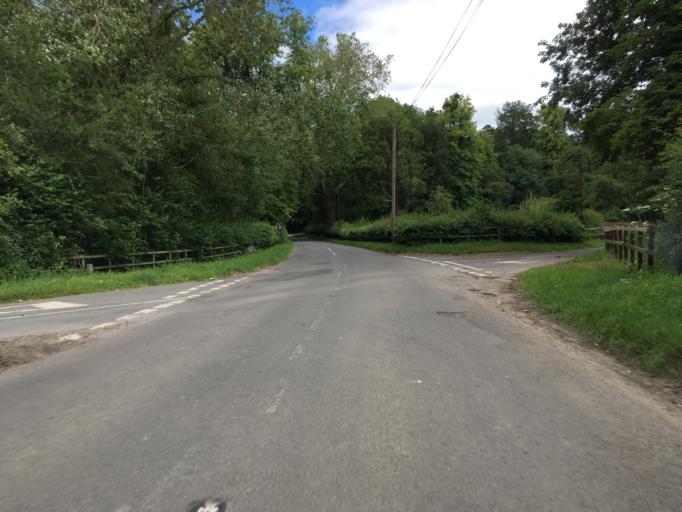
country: GB
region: England
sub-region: West Berkshire
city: Welford
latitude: 51.4567
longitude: -1.4106
